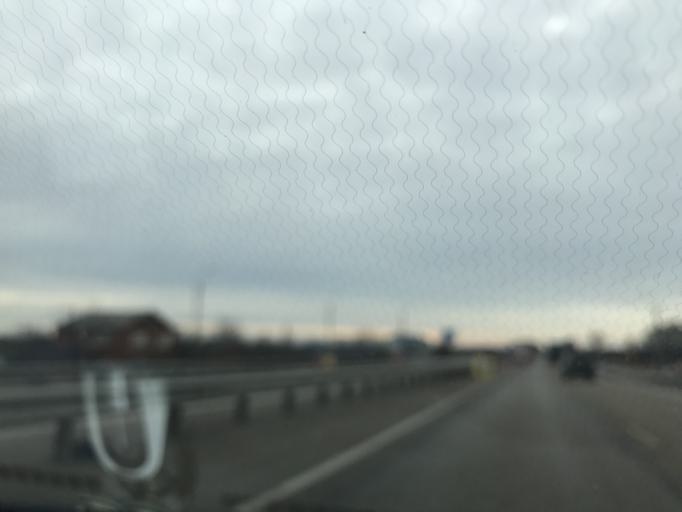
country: RU
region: Krasnodarskiy
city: Glubokiy
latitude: 44.9646
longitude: 41.0612
